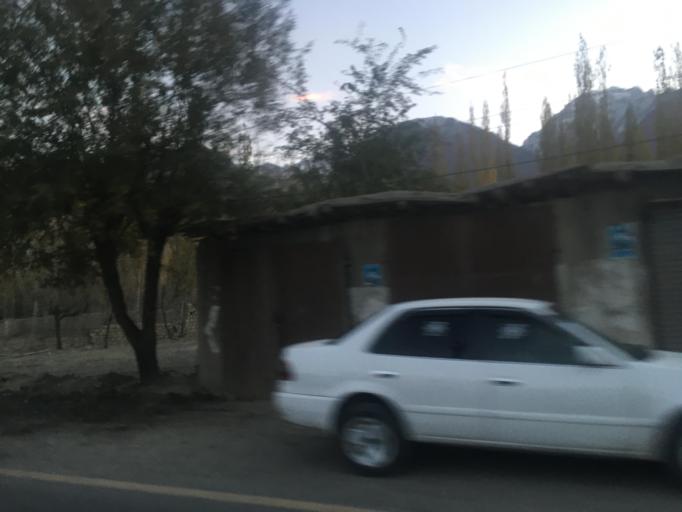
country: PK
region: Gilgit-Baltistan
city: Skardu
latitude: 35.3020
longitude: 75.5516
